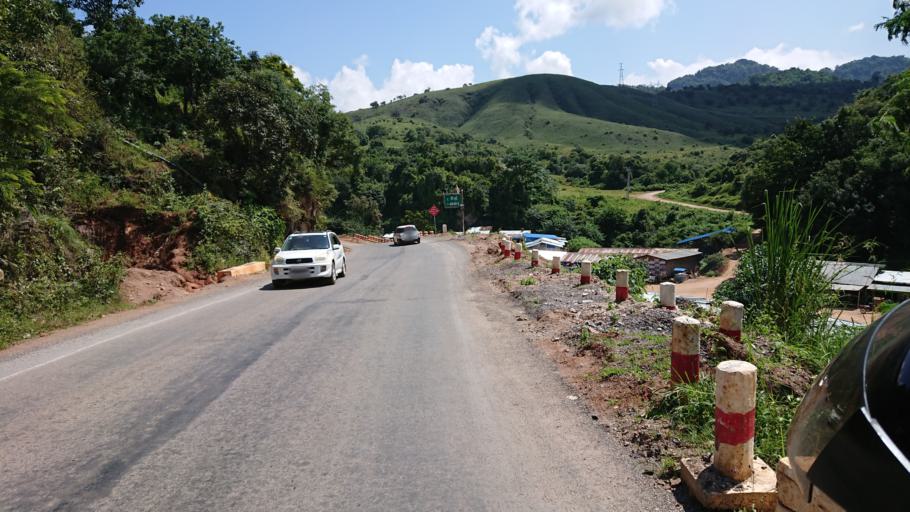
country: MM
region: Shan
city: Taunggyi
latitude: 20.8162
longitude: 97.3337
